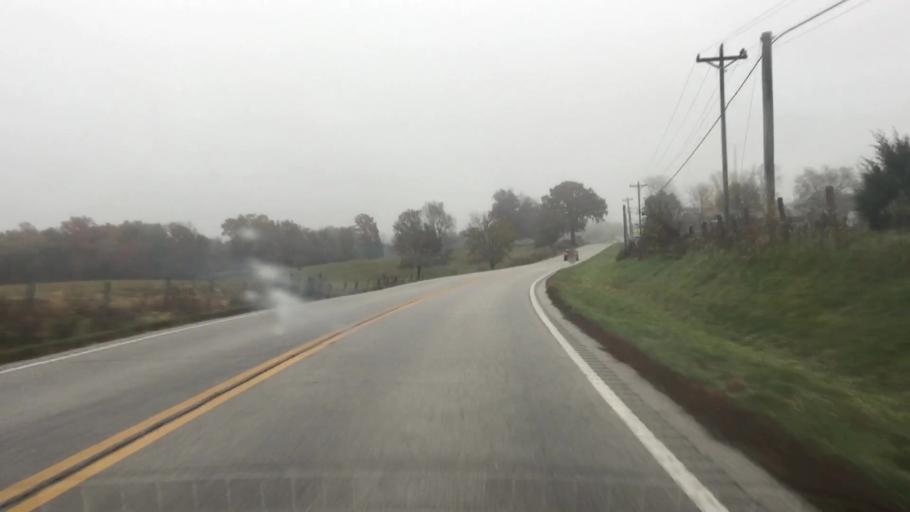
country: US
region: Missouri
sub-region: Callaway County
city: Fulton
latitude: 38.8629
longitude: -92.0062
